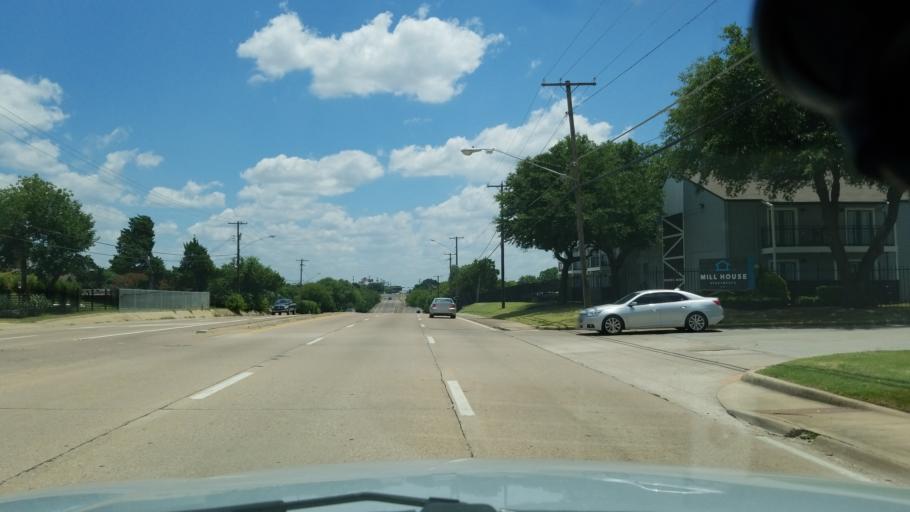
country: US
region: Texas
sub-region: Dallas County
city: Cockrell Hill
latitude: 32.6912
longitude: -96.8642
